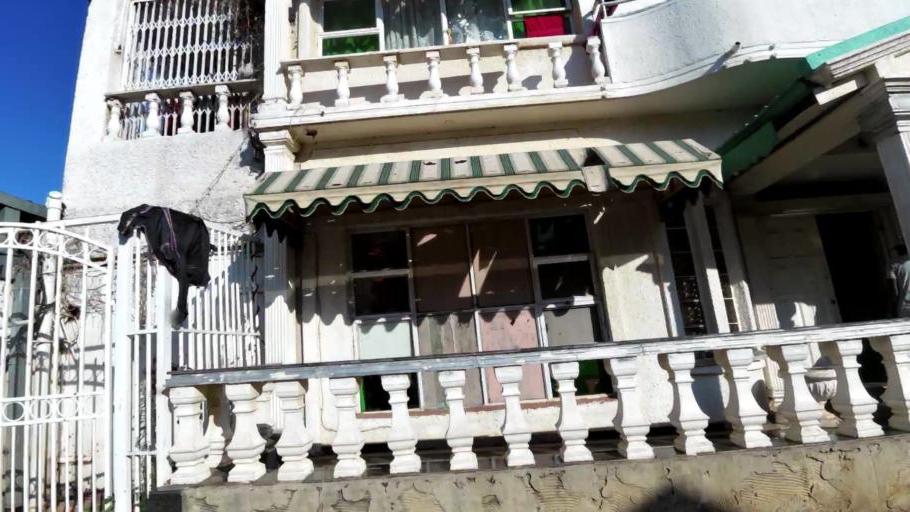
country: ZA
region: Gauteng
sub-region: City of Johannesburg Metropolitan Municipality
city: Johannesburg
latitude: -26.1964
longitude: 28.0172
